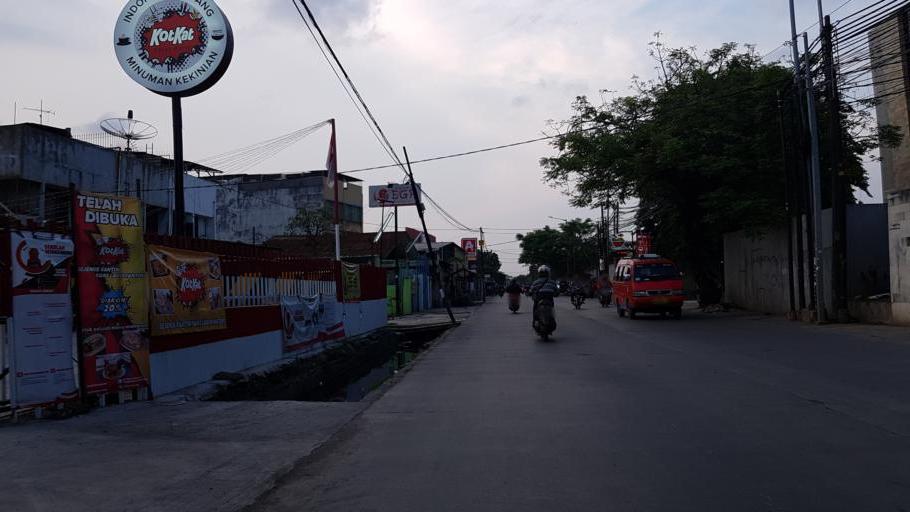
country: ID
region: West Java
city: Teluknaga
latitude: -6.1291
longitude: 106.7427
